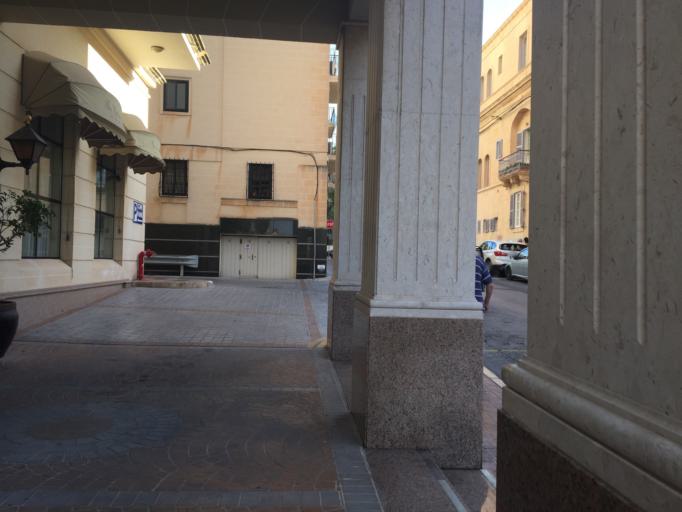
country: MT
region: Tas-Sliema
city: Sliema
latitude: 35.9127
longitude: 14.5026
